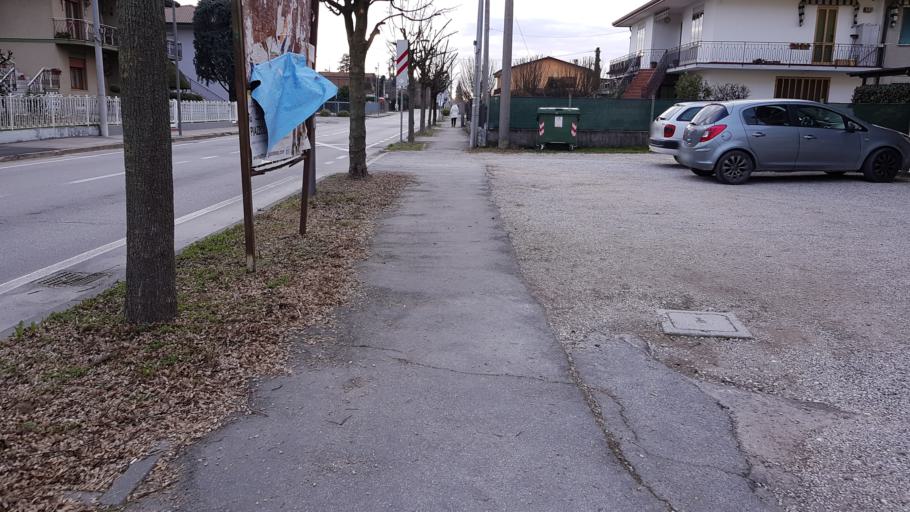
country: IT
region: Veneto
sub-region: Provincia di Padova
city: San Giorgio delle Pertiche
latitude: 45.5414
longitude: 11.9150
